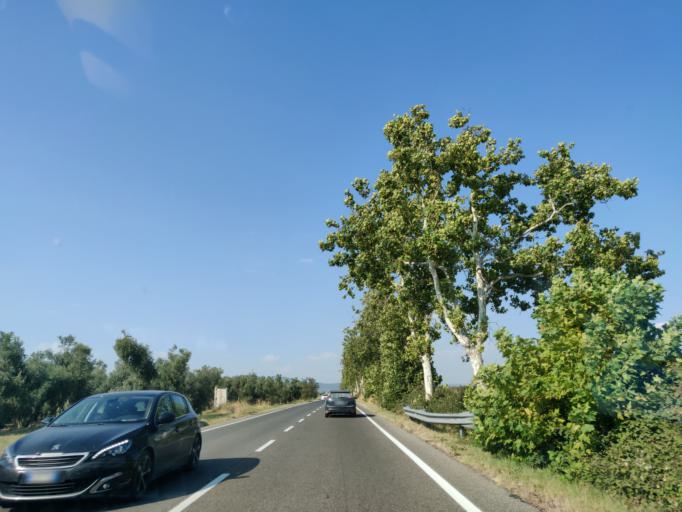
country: IT
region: Latium
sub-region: Provincia di Viterbo
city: Montalto di Castro
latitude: 42.3840
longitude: 11.6605
